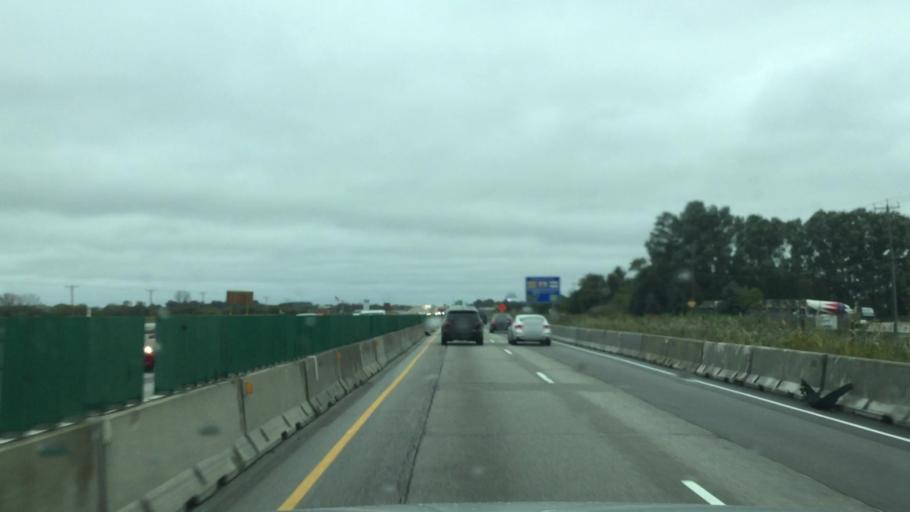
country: US
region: Wisconsin
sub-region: Kenosha County
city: Somers
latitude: 42.6267
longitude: -87.9527
